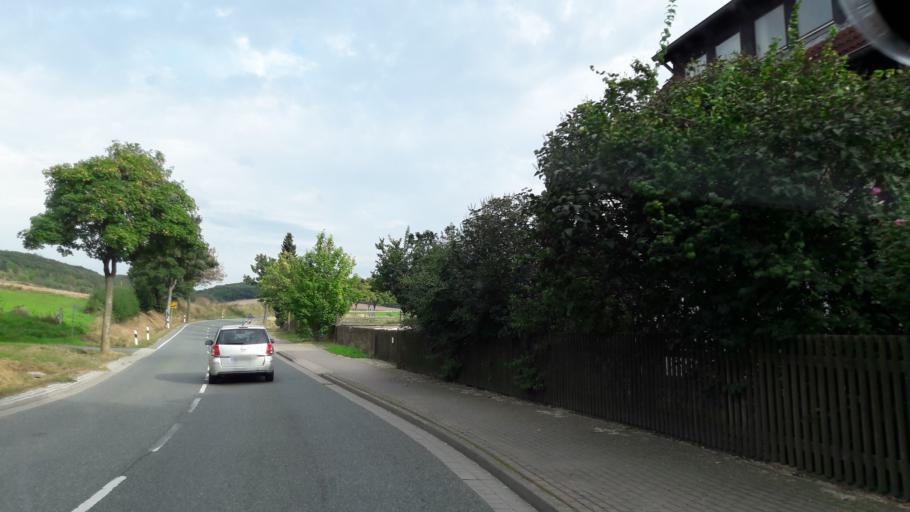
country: DE
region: Lower Saxony
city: Bad Salzdetfurth
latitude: 52.0806
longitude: 10.0353
